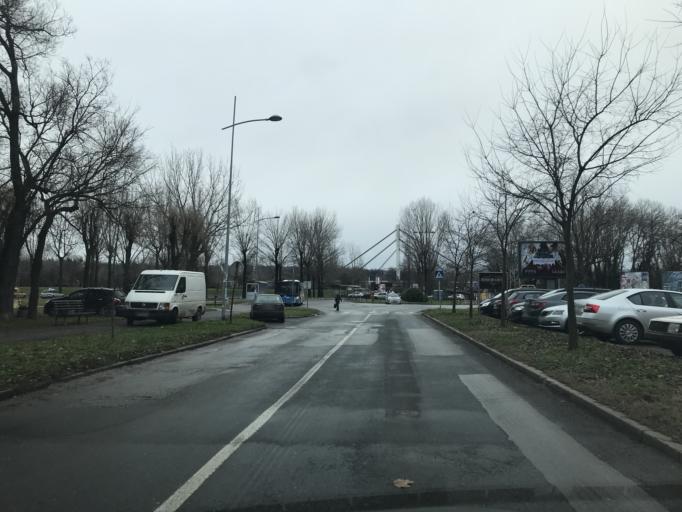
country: RS
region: Autonomna Pokrajina Vojvodina
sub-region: Juznobacki Okrug
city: Novi Sad
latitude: 45.2397
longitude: 19.8481
